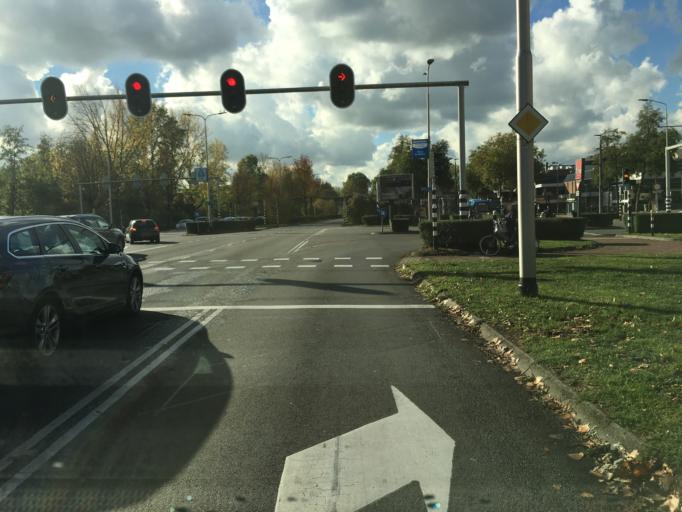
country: NL
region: Gelderland
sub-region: Gemeente Arnhem
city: Arnhem
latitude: 51.9588
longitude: 5.9001
